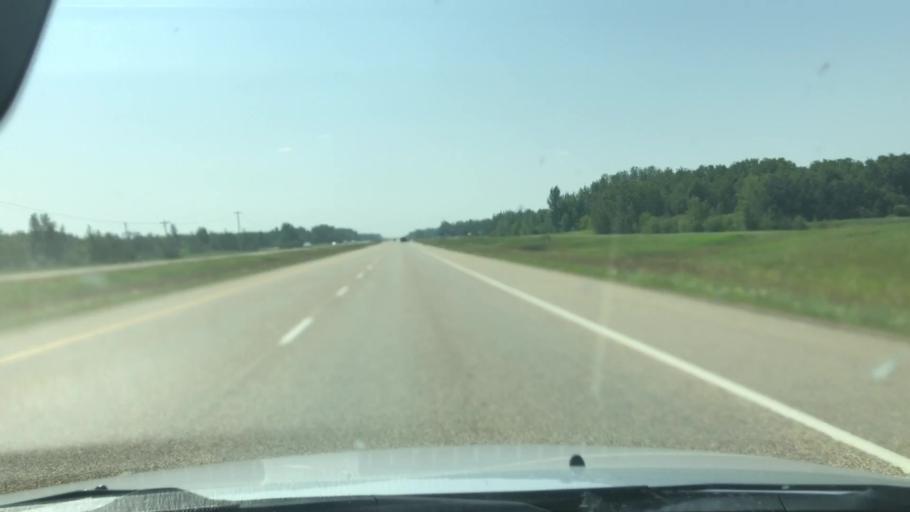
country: CA
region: Alberta
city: Devon
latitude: 53.4301
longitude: -113.7632
